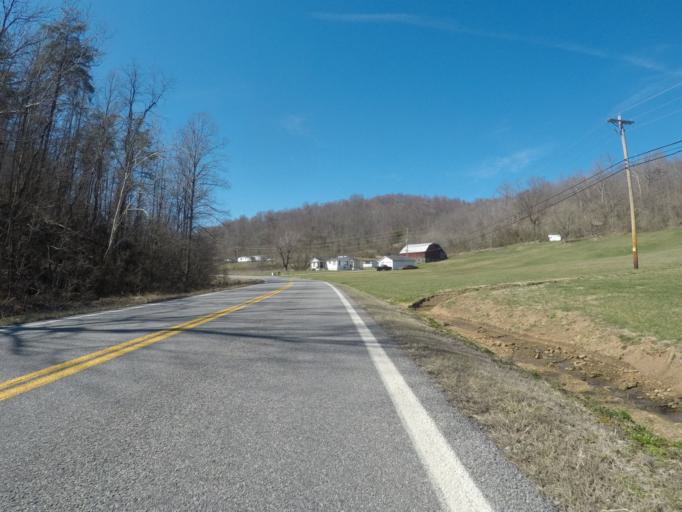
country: US
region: Ohio
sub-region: Lawrence County
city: Burlington
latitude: 38.4972
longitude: -82.5244
